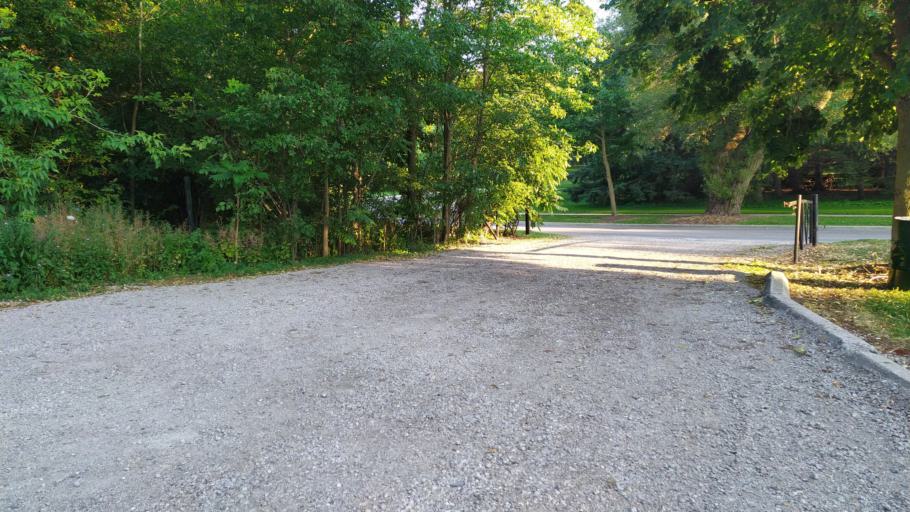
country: CA
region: Ontario
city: Stratford
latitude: 43.3764
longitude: -80.9648
